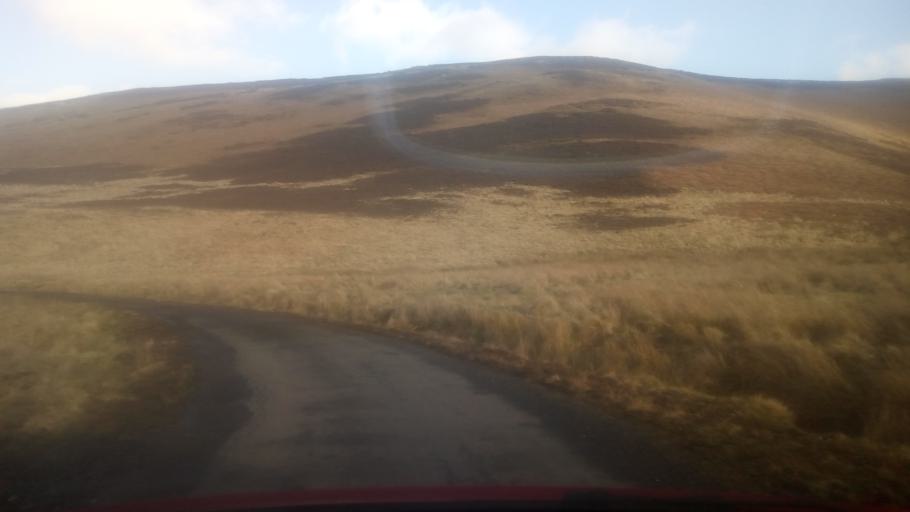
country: GB
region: Scotland
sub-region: The Scottish Borders
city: Kelso
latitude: 55.4313
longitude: -2.3633
